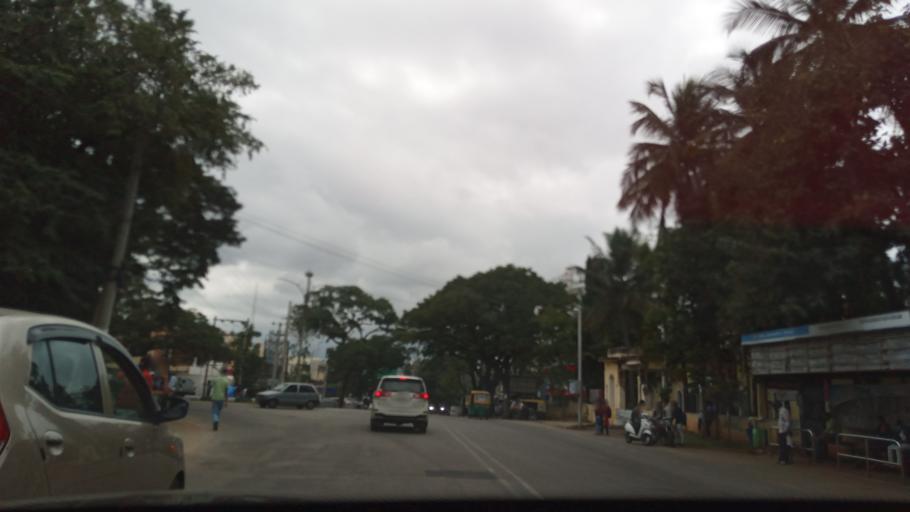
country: IN
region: Karnataka
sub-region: Mysore
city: Mysore
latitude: 12.3040
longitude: 76.6354
